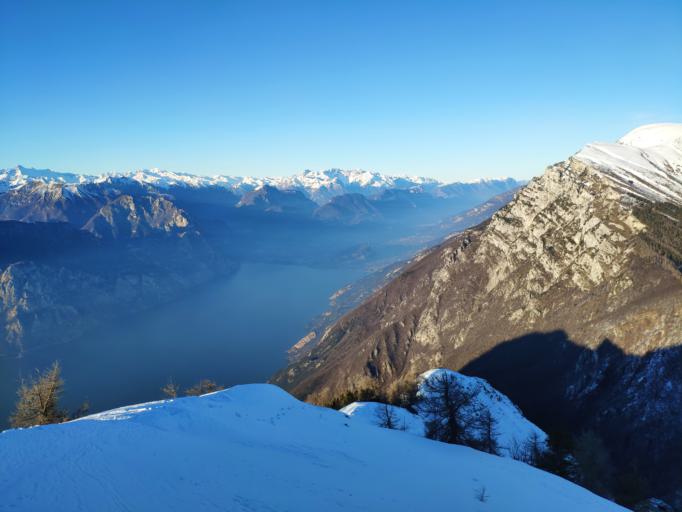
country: IT
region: Veneto
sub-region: Provincia di Verona
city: Malcesine
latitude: 45.7813
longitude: 10.8622
